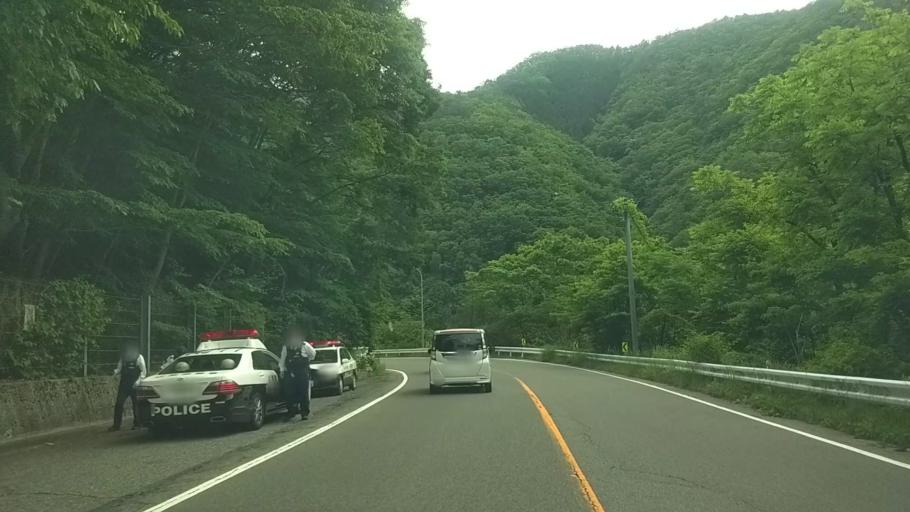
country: JP
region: Yamanashi
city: Fujikawaguchiko
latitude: 35.5378
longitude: 138.5936
